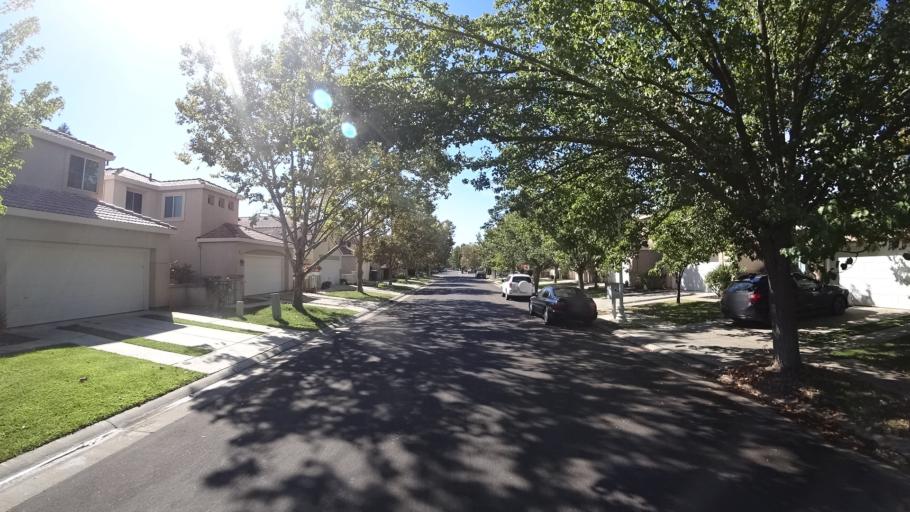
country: US
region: California
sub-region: Sacramento County
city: Laguna
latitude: 38.4263
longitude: -121.4748
